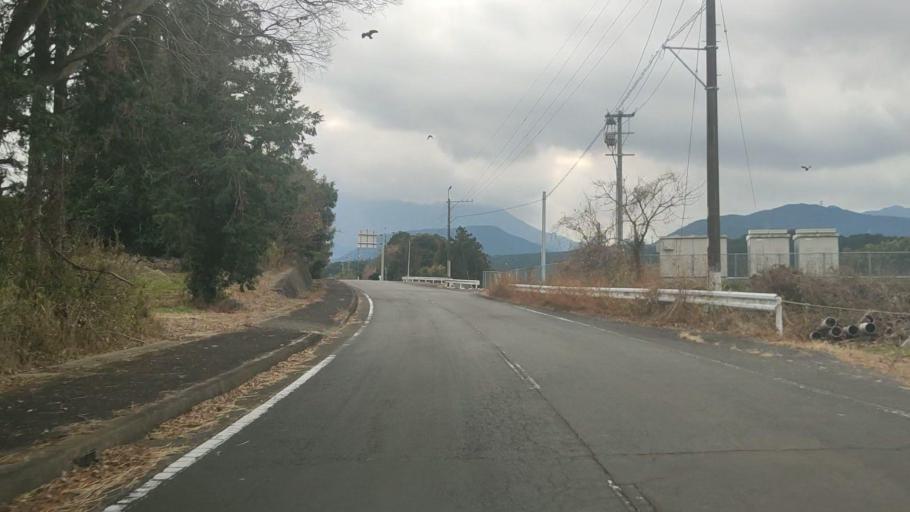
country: JP
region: Nagasaki
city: Shimabara
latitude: 32.8224
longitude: 130.2909
